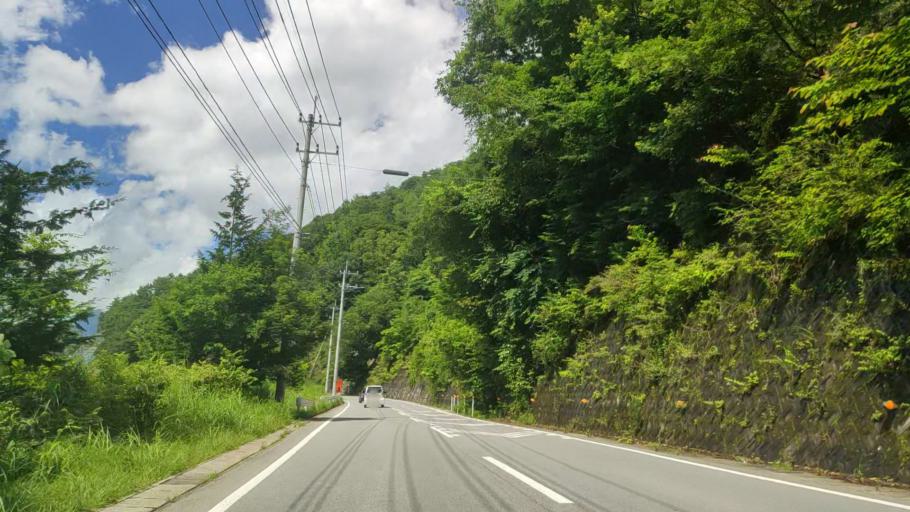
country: JP
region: Yamanashi
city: Enzan
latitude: 35.8283
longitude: 138.7649
